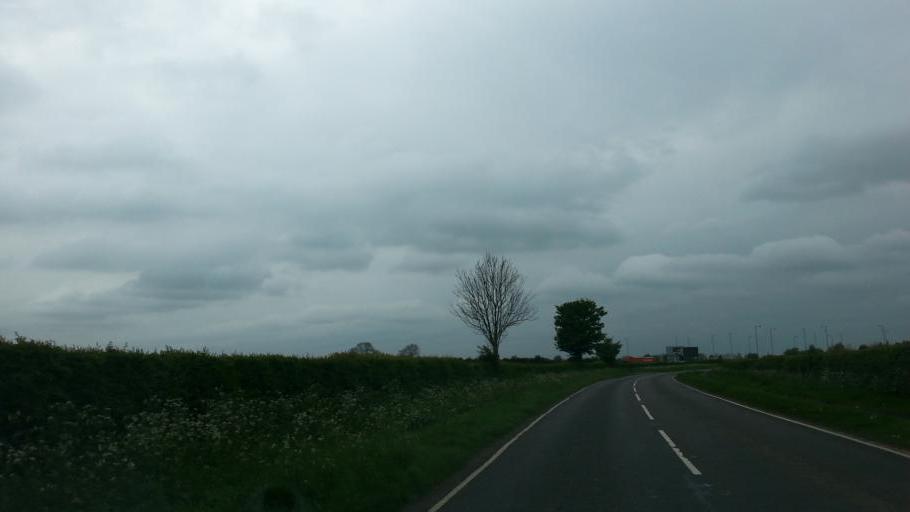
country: GB
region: England
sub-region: Lincolnshire
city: Grantham
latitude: 52.8953
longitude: -0.5872
